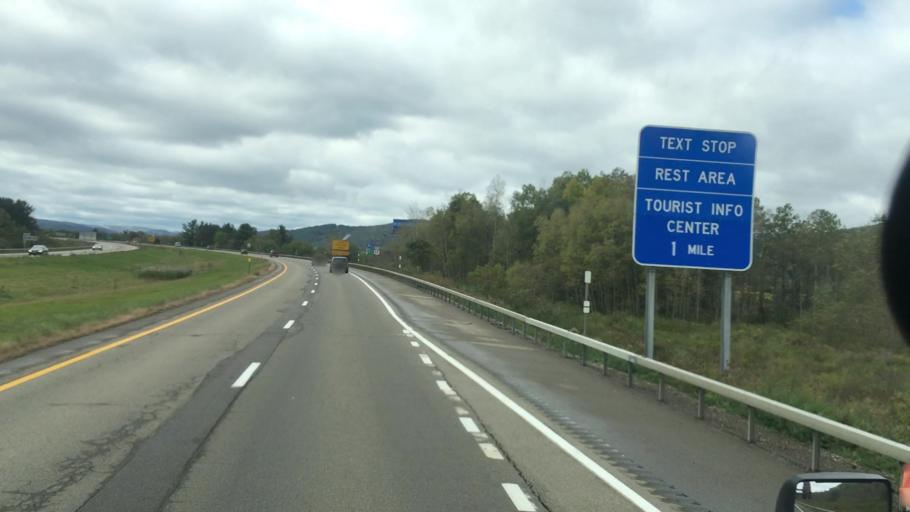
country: US
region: New York
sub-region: Cattaraugus County
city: Allegany
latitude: 42.1029
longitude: -78.5148
